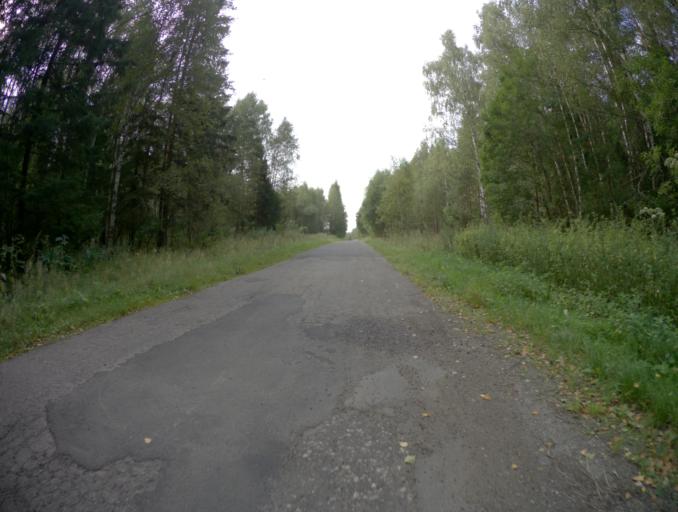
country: RU
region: Vladimir
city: Golovino
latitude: 55.9690
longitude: 40.4011
